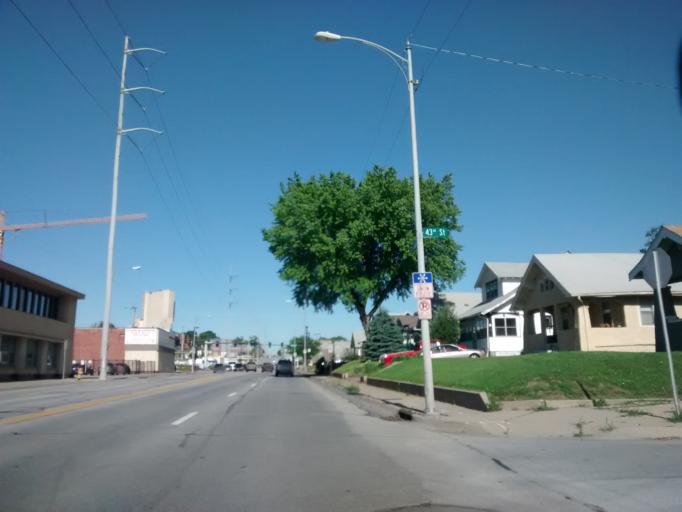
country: US
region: Nebraska
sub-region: Douglas County
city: Omaha
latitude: 41.2524
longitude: -95.9776
